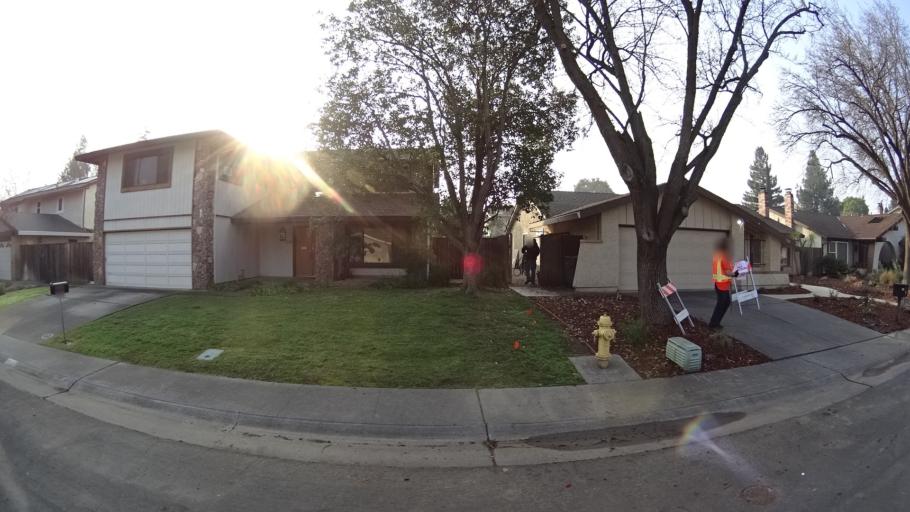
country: US
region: California
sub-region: Yolo County
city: Davis
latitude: 38.5673
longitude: -121.7516
